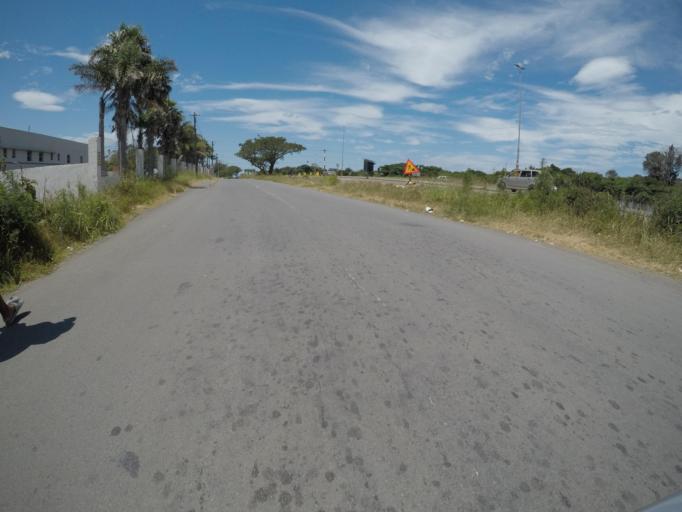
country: ZA
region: Eastern Cape
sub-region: Buffalo City Metropolitan Municipality
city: East London
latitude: -33.0350
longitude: 27.8457
